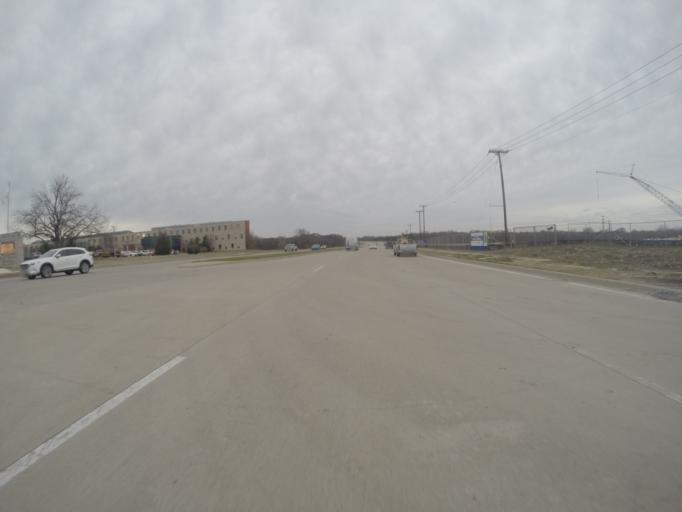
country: US
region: Texas
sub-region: Collin County
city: Saint Paul
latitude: 33.0255
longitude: -96.5689
